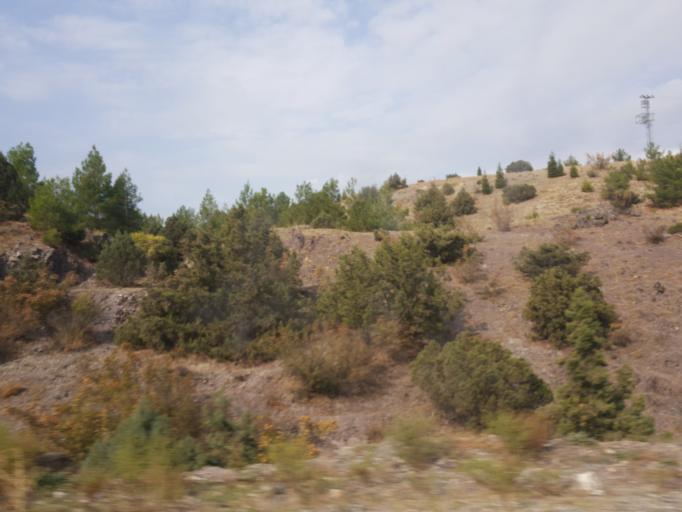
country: TR
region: Corum
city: Kamil
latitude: 41.1107
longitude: 34.7413
